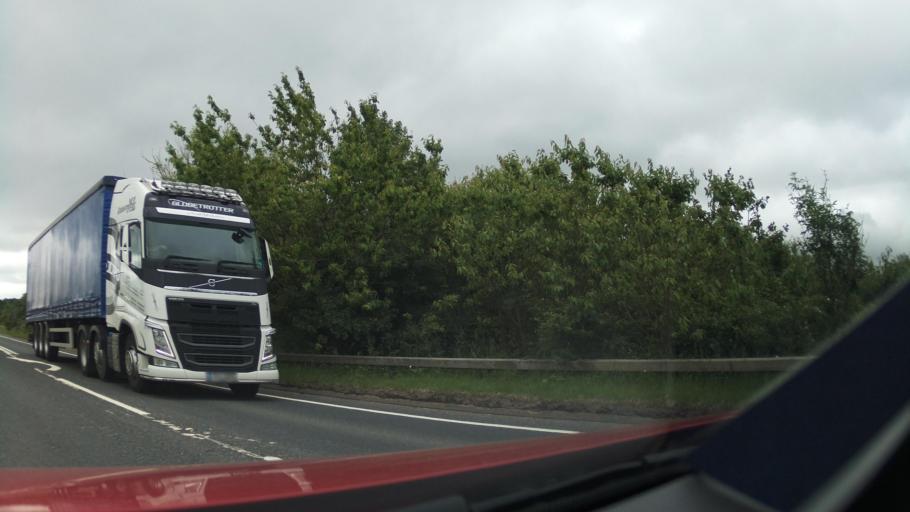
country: GB
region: England
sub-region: Leicestershire
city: Ashby de la Zouch
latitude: 52.7464
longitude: -1.4431
